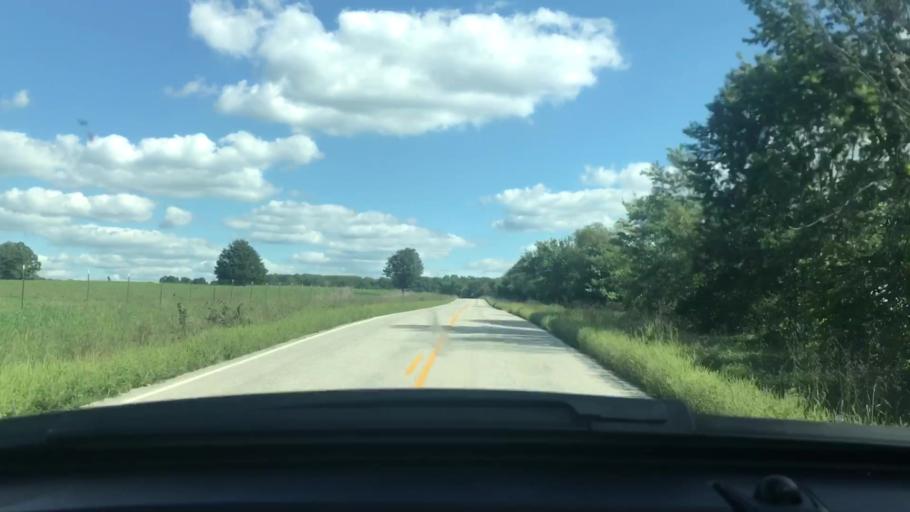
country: US
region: Missouri
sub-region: Wright County
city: Hartville
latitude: 37.3805
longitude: -92.4369
